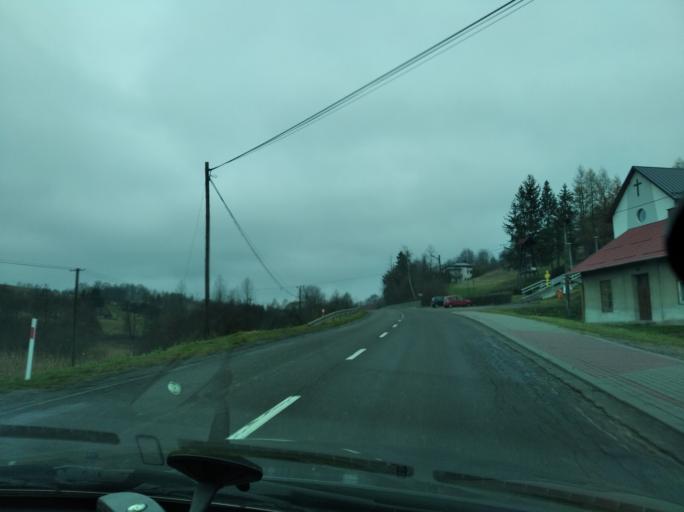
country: PL
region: Subcarpathian Voivodeship
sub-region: Powiat przeworski
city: Jawornik Polski
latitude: 49.8801
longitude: 22.2429
